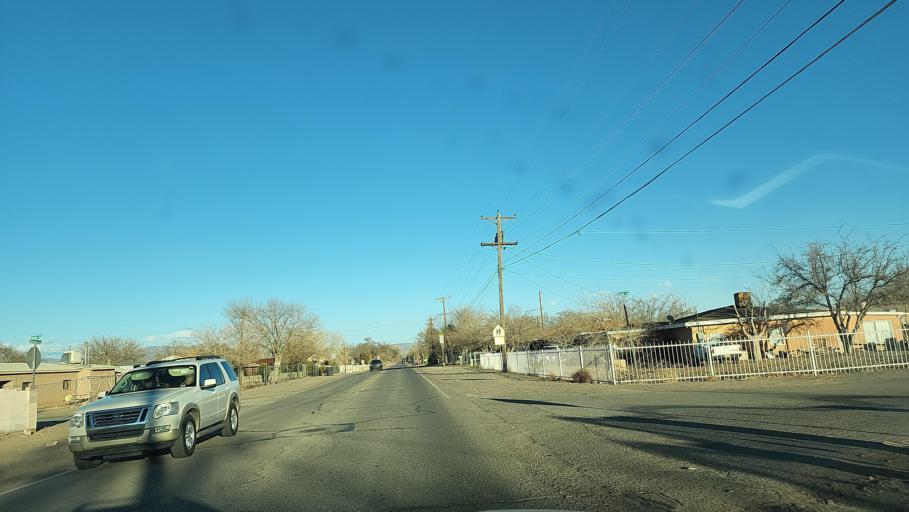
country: US
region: New Mexico
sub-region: Bernalillo County
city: South Valley
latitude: 35.0305
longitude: -106.7115
